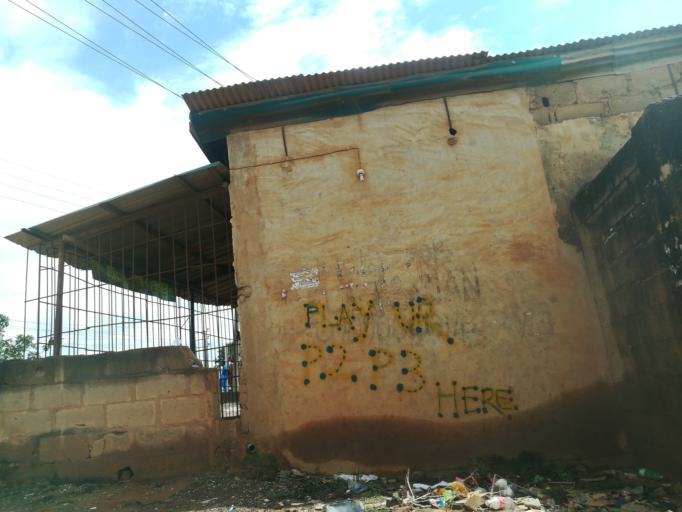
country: NG
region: Lagos
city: Ikorodu
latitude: 6.6385
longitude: 3.5136
